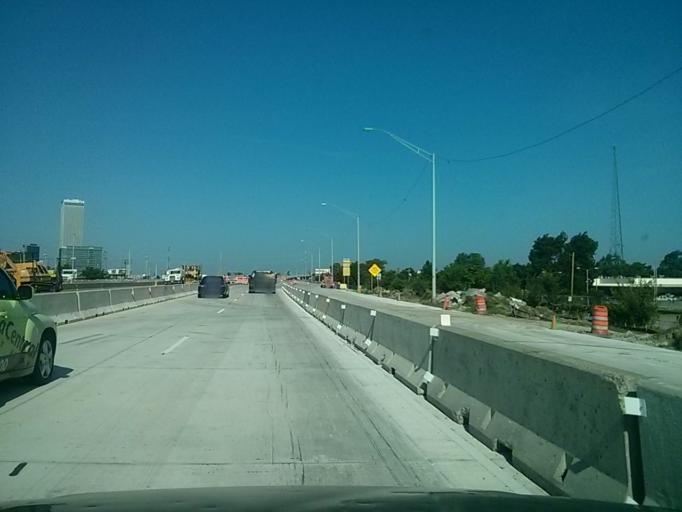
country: US
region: Oklahoma
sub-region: Tulsa County
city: Tulsa
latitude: 36.1594
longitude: -95.9726
